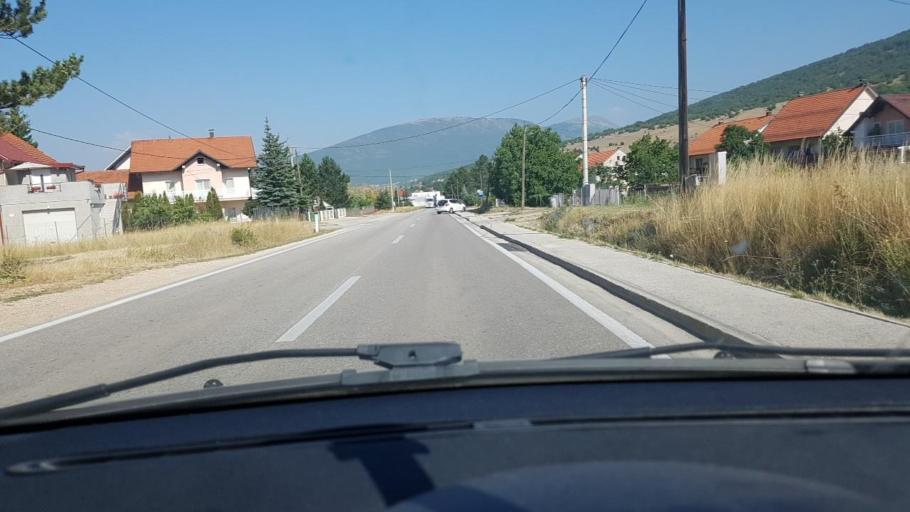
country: BA
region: Federation of Bosnia and Herzegovina
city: Livno
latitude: 43.8489
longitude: 16.9550
